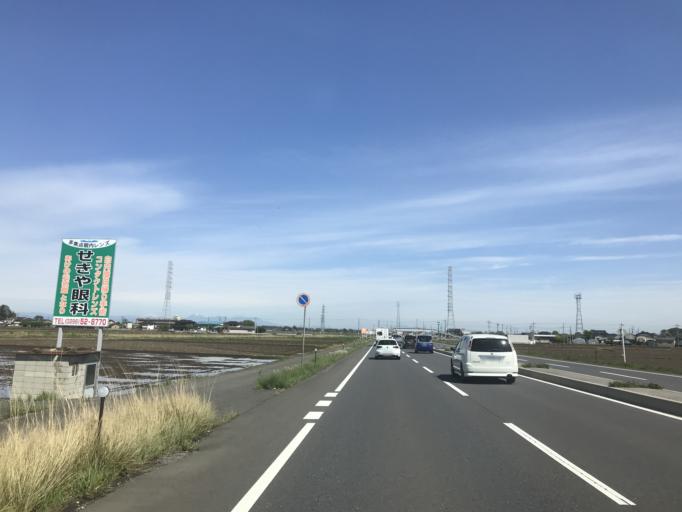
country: JP
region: Ibaraki
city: Ishige
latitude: 36.1687
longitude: 139.9930
